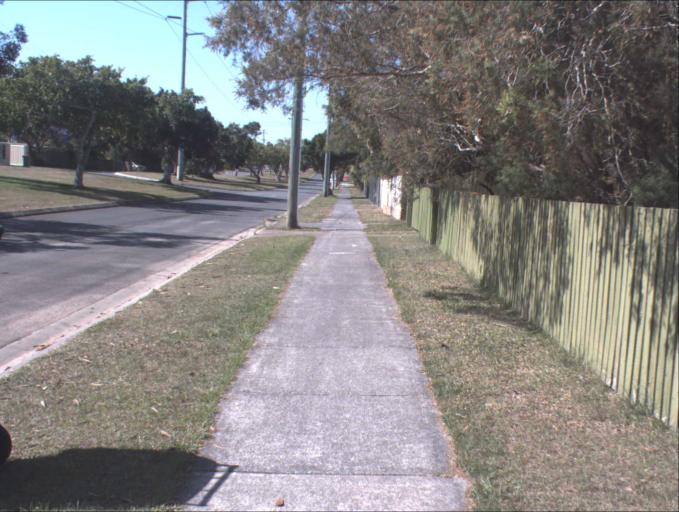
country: AU
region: Queensland
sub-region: Logan
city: Beenleigh
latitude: -27.6967
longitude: 153.2094
